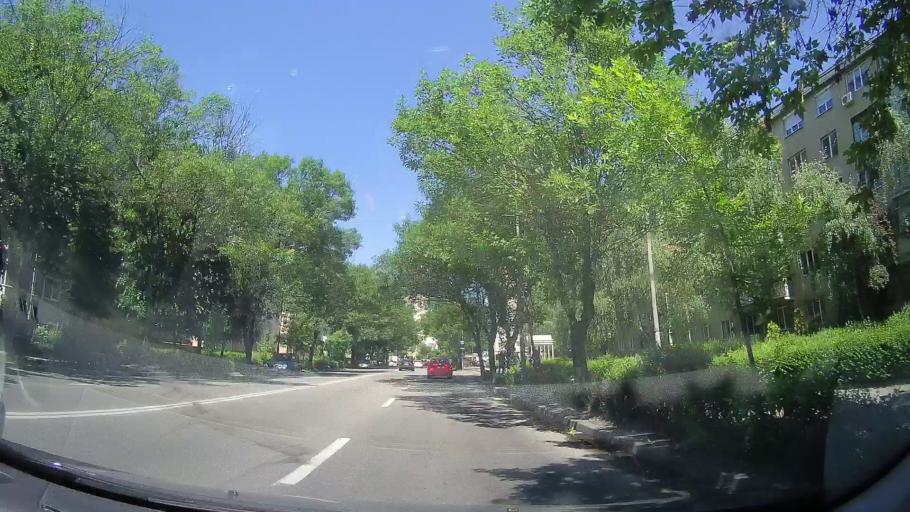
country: RO
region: Arges
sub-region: Comuna Albestii de Arges
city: Pitesti
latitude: 44.8687
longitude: 24.8584
